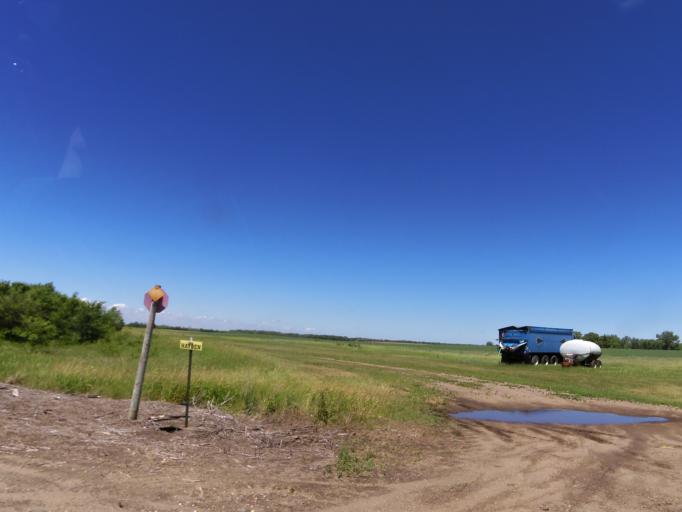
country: US
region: Minnesota
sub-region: Otter Tail County
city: Perham
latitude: 46.6291
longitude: -95.6256
